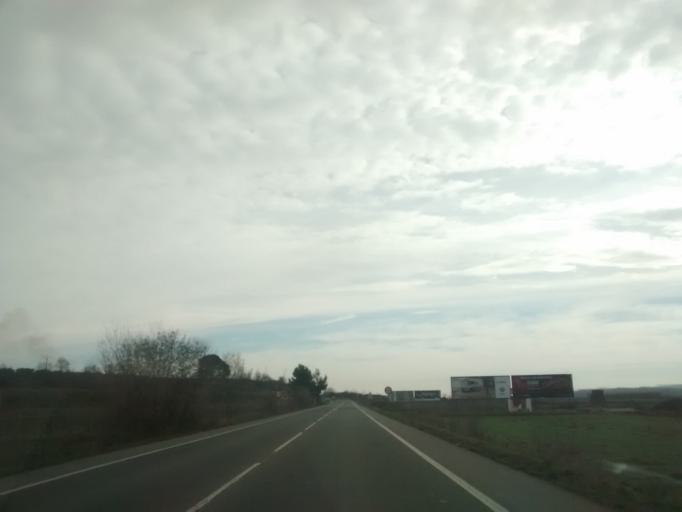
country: ES
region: Navarre
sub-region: Provincia de Navarra
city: Viana
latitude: 42.4750
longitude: -2.3773
